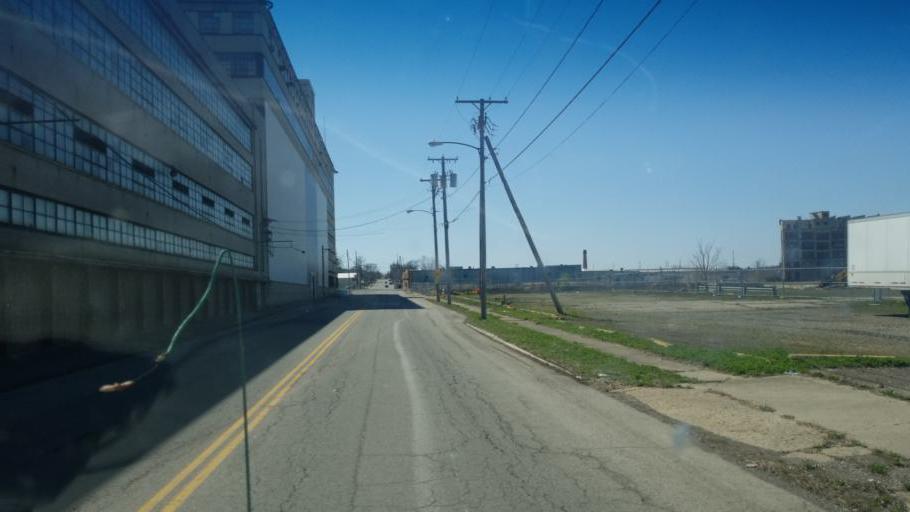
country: US
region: Ohio
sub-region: Richland County
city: Mansfield
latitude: 40.7607
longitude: -82.5053
